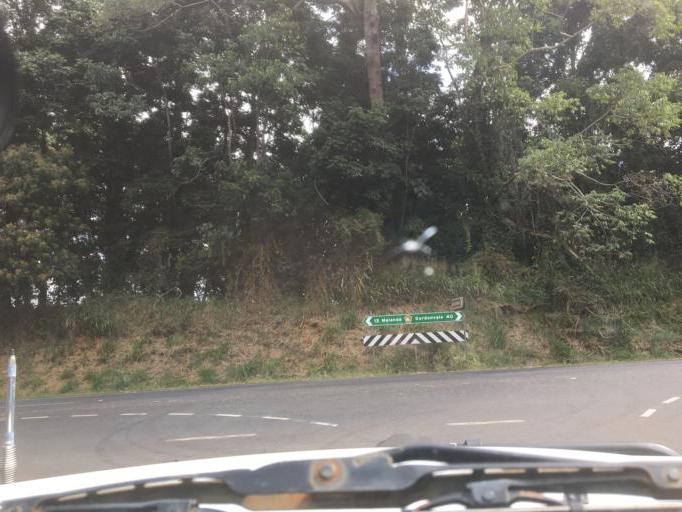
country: AU
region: Queensland
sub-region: Tablelands
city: Atherton
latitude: -17.2834
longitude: 145.6127
